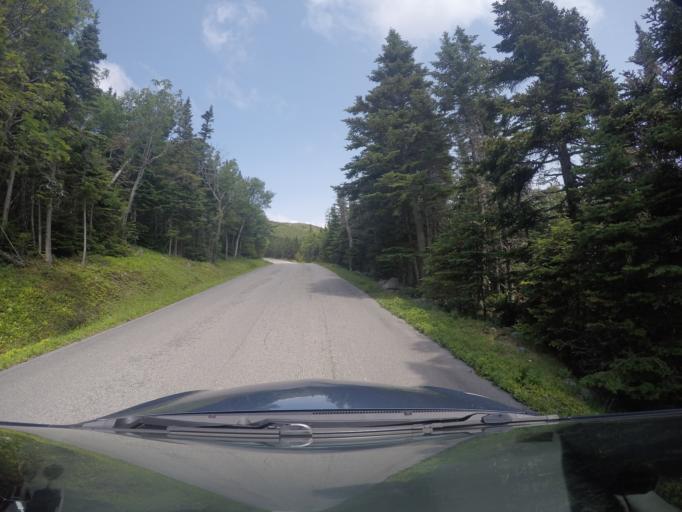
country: US
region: New Hampshire
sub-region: Coos County
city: Gorham
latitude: 44.2922
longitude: -71.2748
